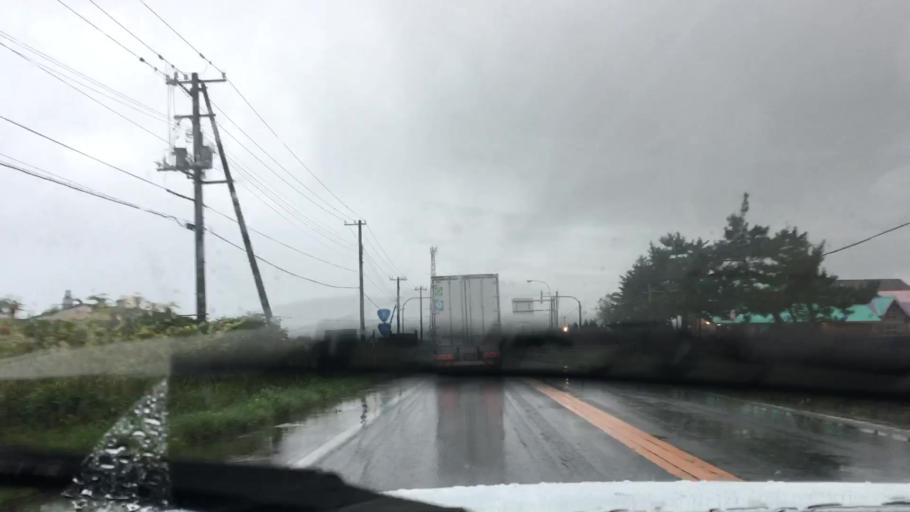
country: JP
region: Hokkaido
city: Niseko Town
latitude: 42.4751
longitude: 140.3466
